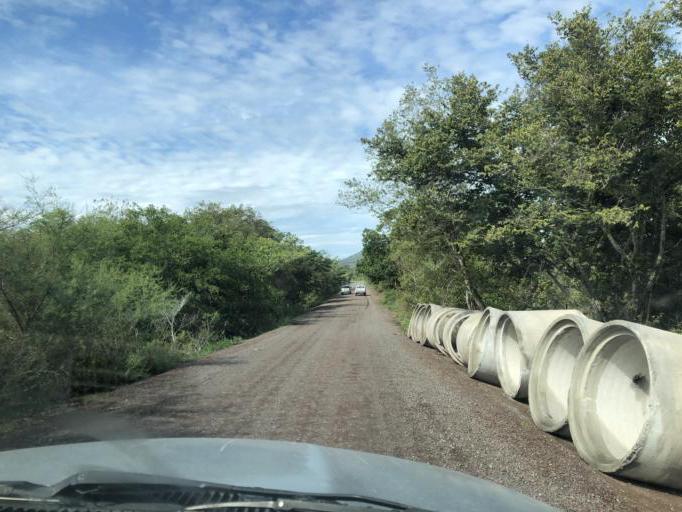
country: MX
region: Veracruz
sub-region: Alto Lucero de Gutierrez Barrios
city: Palma Sola
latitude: 19.7934
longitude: -96.5492
